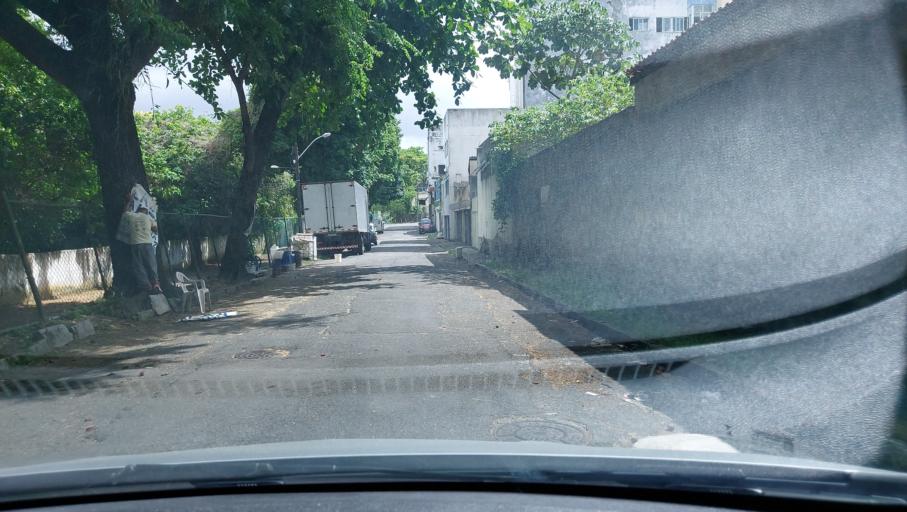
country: BR
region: Bahia
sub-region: Salvador
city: Salvador
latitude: -12.9775
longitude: -38.4973
